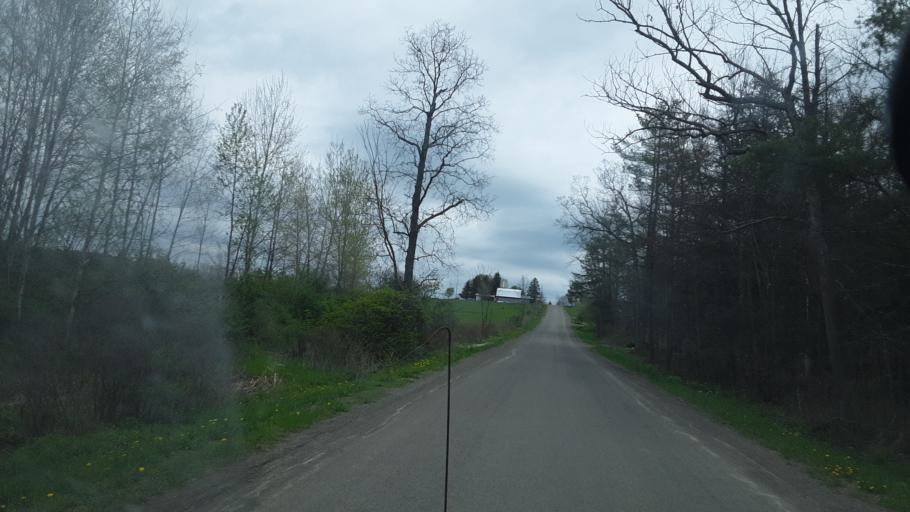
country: US
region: New York
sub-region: Steuben County
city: Addison
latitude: 42.0926
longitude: -77.2962
